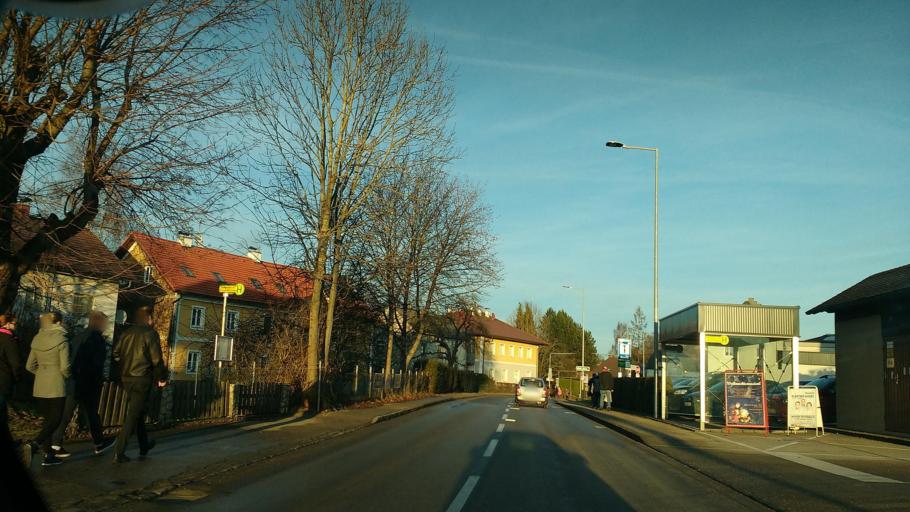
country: AT
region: Upper Austria
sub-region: Politischer Bezirk Gmunden
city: Scharnstein
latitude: 47.9590
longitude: 14.0149
